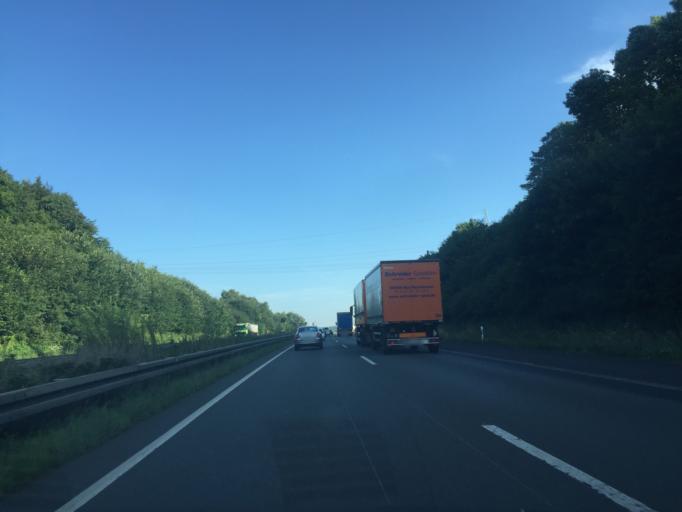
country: DE
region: North Rhine-Westphalia
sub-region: Regierungsbezirk Arnsberg
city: Luedenscheid
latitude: 51.2109
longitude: 7.6710
